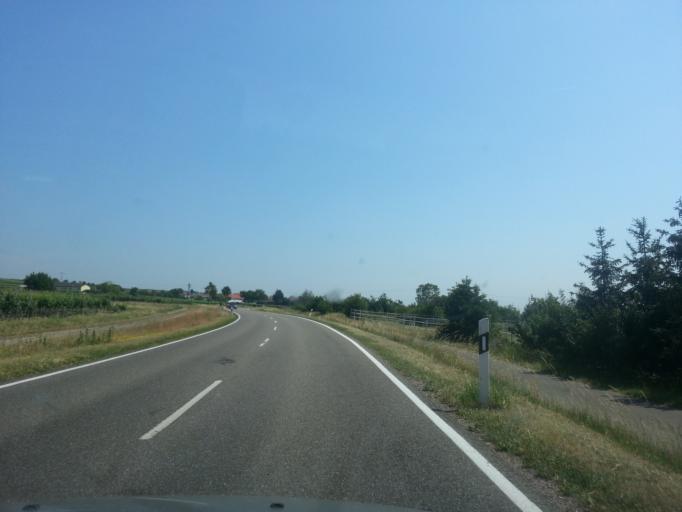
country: DE
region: Rheinland-Pfalz
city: Weisenheim am Sand
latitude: 49.5168
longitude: 8.2316
